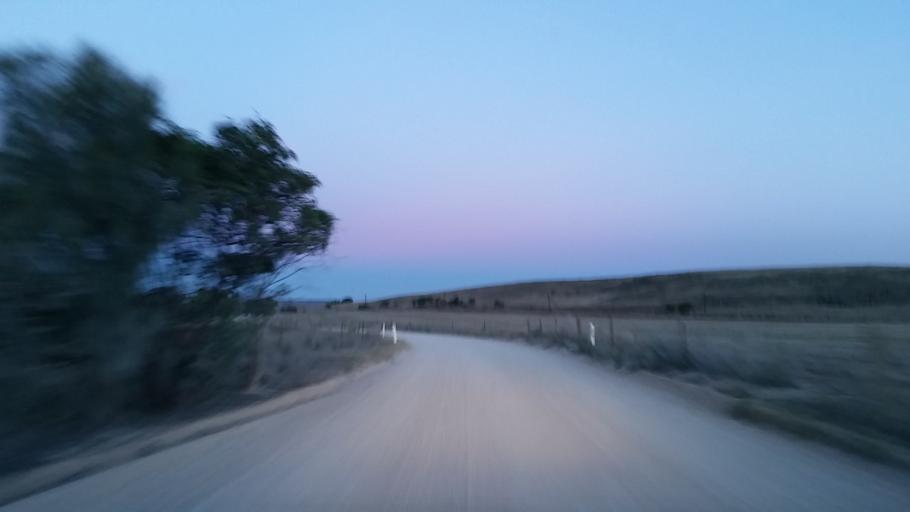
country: AU
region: South Australia
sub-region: Mount Barker
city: Callington
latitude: -35.1051
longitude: 139.0063
